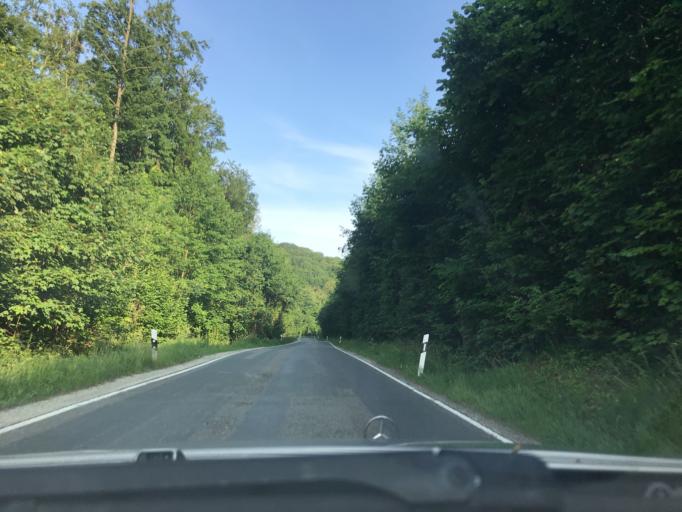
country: DE
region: Thuringia
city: Kleinbartloff
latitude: 51.3430
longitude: 10.3677
